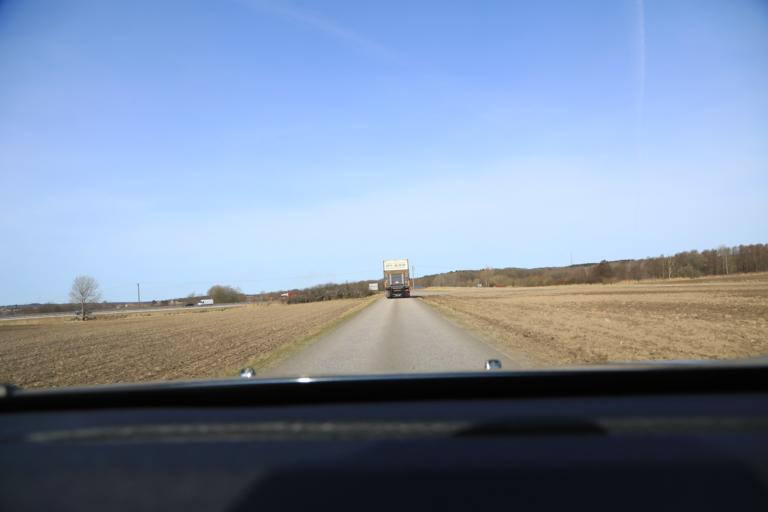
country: SE
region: Halland
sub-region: Kungsbacka Kommun
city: Frillesas
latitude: 57.2556
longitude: 12.2197
